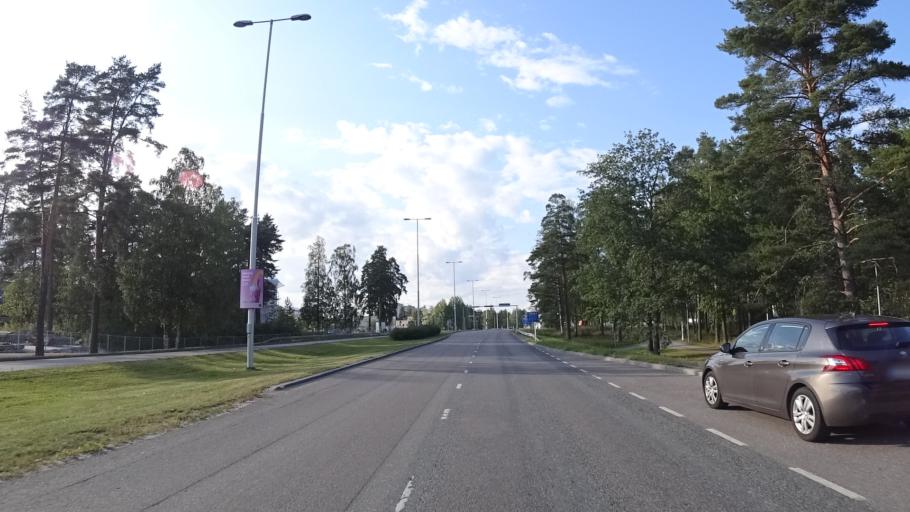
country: FI
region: South Karelia
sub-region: Imatra
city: Imatra
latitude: 61.1832
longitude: 28.7802
